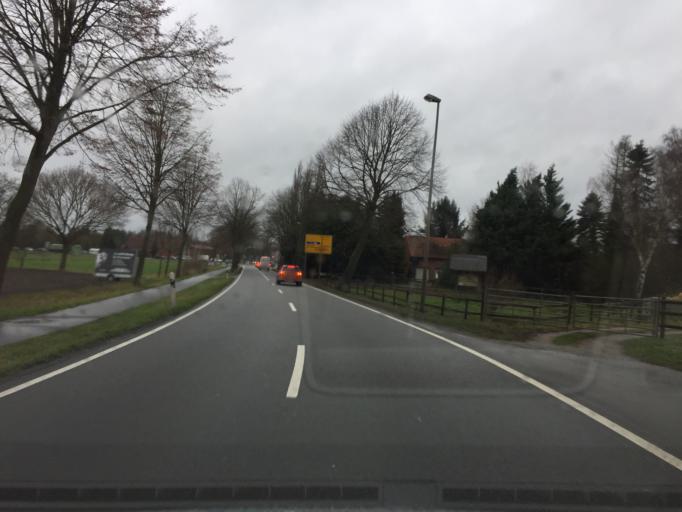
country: DE
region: Lower Saxony
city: Stuhr
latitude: 52.9929
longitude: 8.7181
